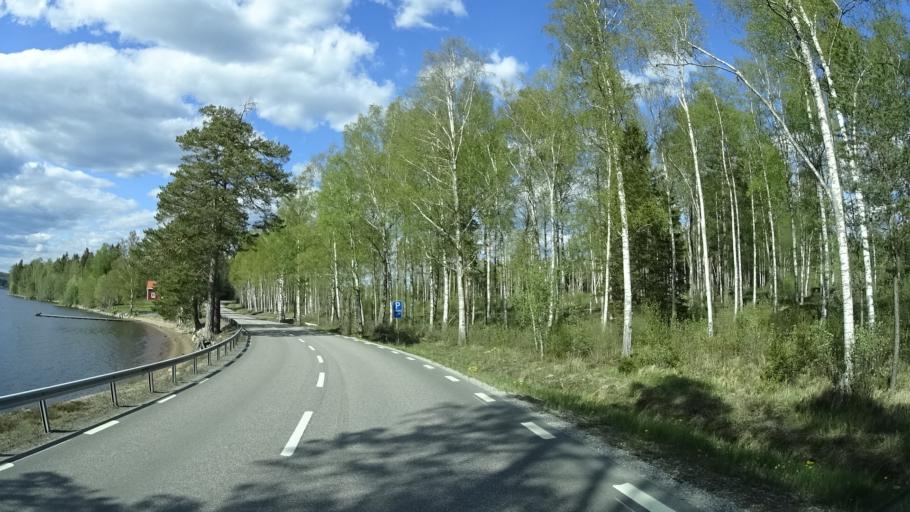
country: SE
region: OErebro
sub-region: Nora Kommun
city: As
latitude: 59.4990
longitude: 14.9570
